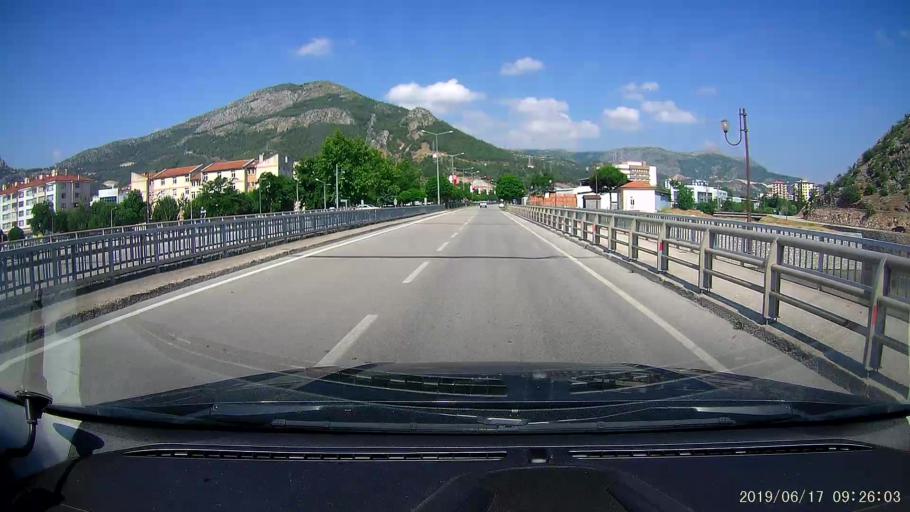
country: TR
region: Amasya
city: Amasya
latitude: 40.6686
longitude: 35.8405
